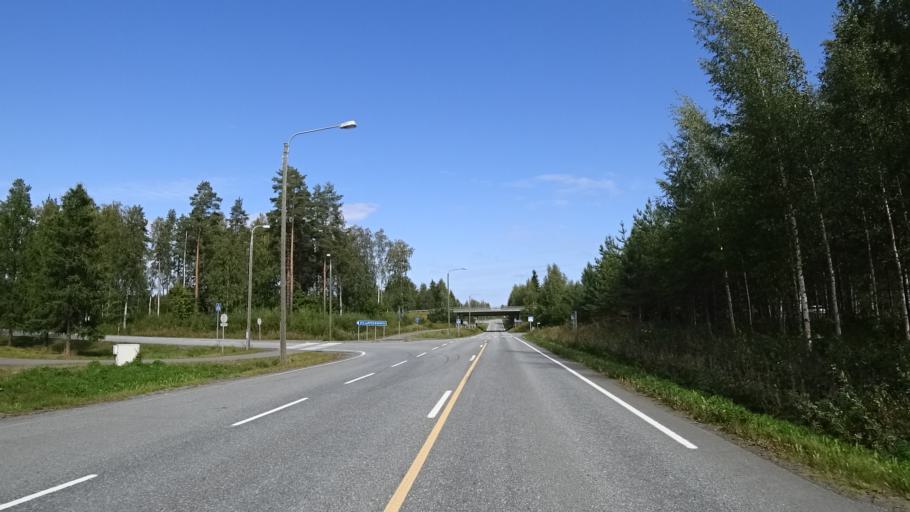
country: FI
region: North Karelia
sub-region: Joensuu
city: Pyhaeselkae
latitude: 62.4757
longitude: 29.9551
